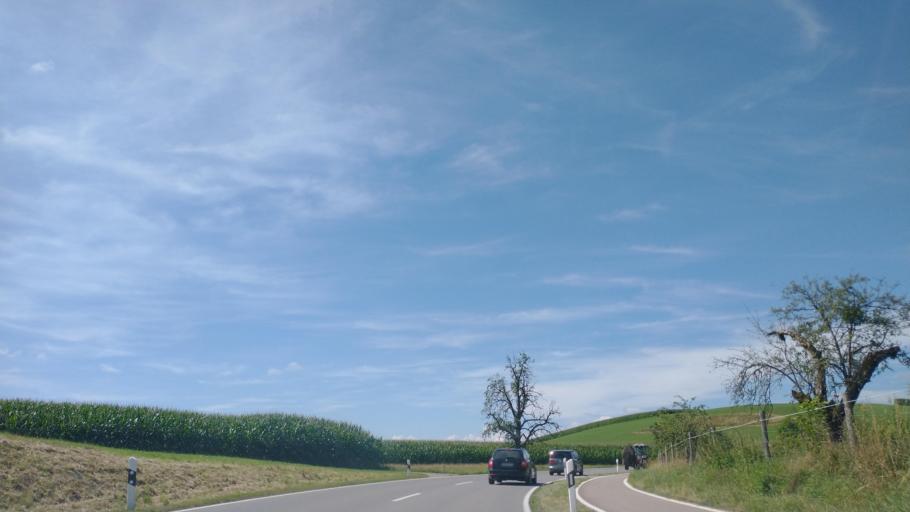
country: DE
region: Baden-Wuerttemberg
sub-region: Tuebingen Region
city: Neukirch
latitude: 47.6656
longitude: 9.7224
